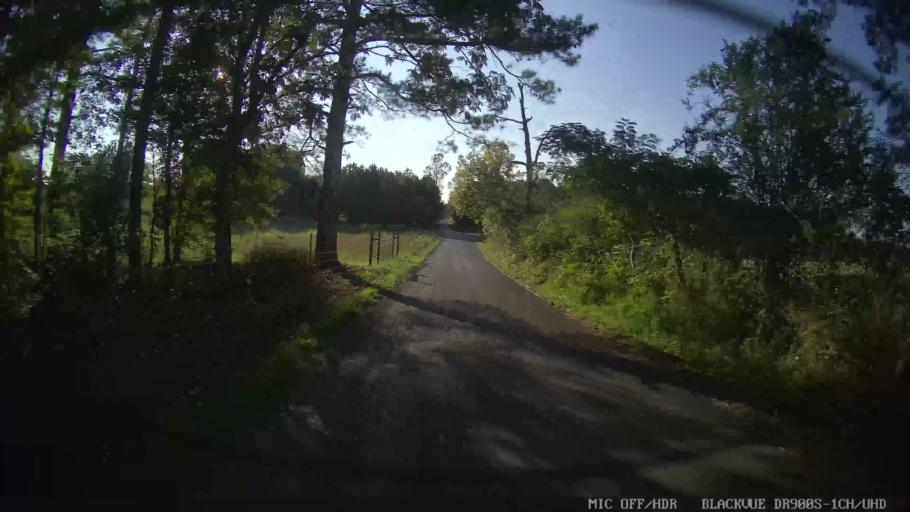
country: US
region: Tennessee
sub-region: Bradley County
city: Wildwood Lake
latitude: 35.0154
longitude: -84.7510
